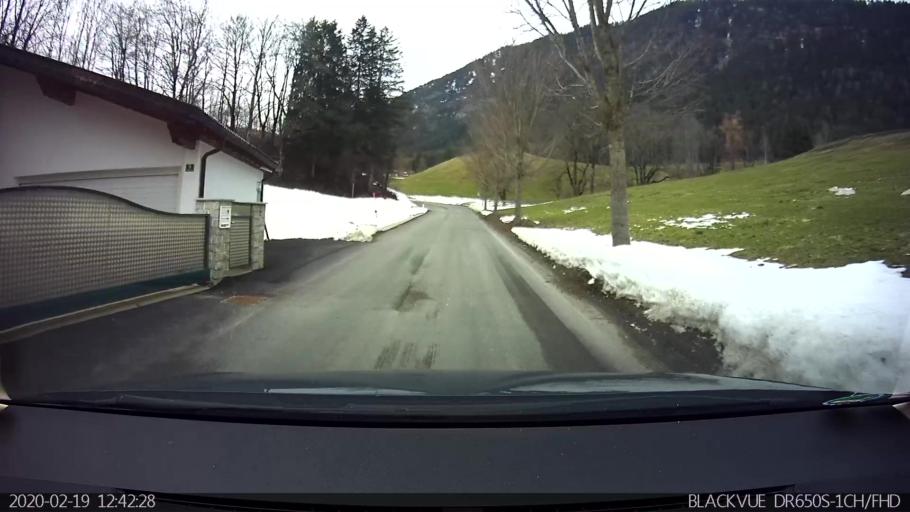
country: AT
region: Tyrol
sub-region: Politischer Bezirk Schwaz
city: Weer
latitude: 47.3283
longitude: 11.6212
